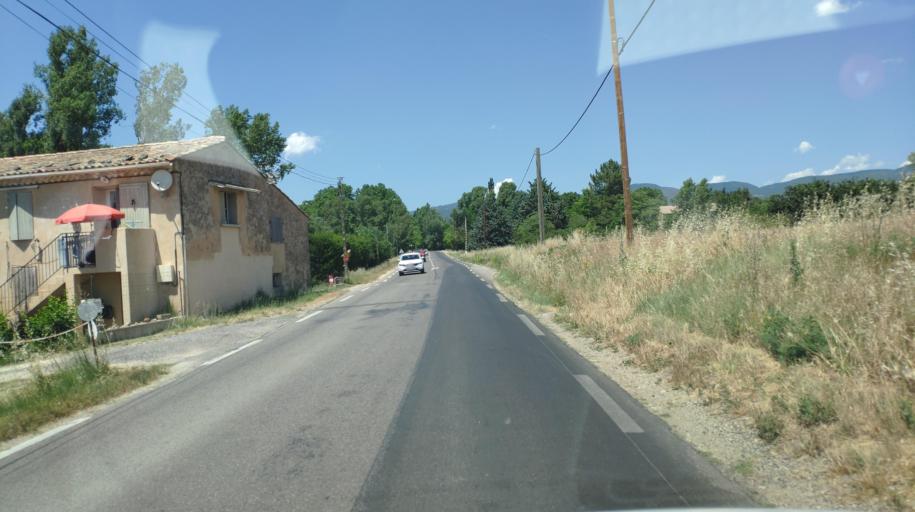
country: FR
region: Provence-Alpes-Cote d'Azur
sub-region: Departement du Vaucluse
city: Apt
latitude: 43.8969
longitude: 5.3833
